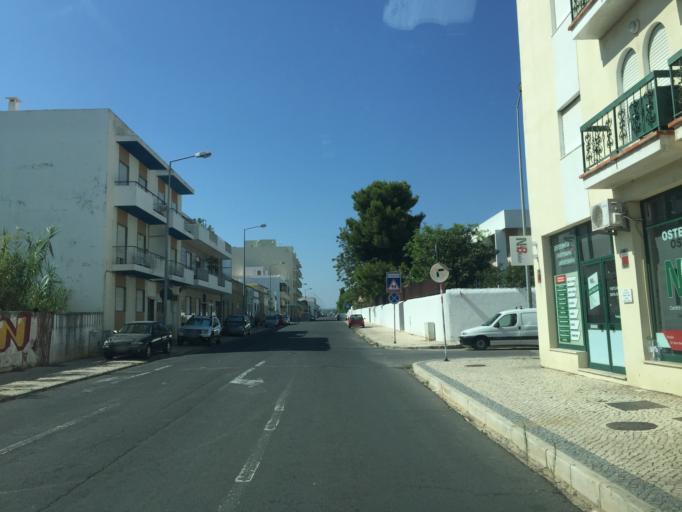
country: PT
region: Faro
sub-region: Olhao
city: Olhao
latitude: 37.0326
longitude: -7.8455
